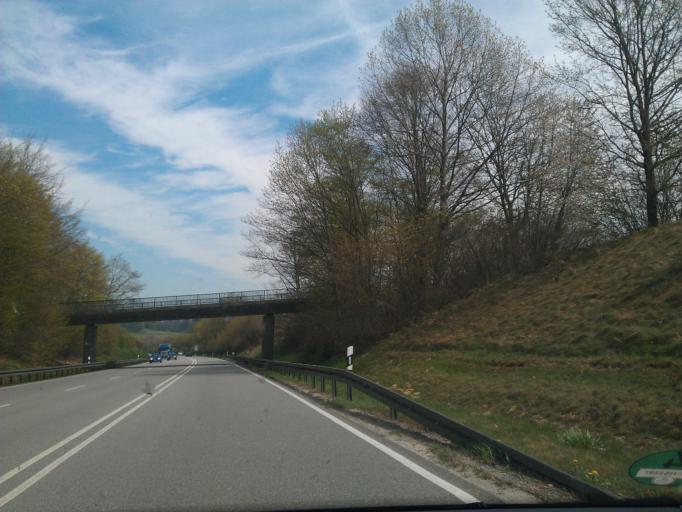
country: DE
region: Bavaria
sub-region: Swabia
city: Aichach
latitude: 48.4358
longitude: 11.1309
